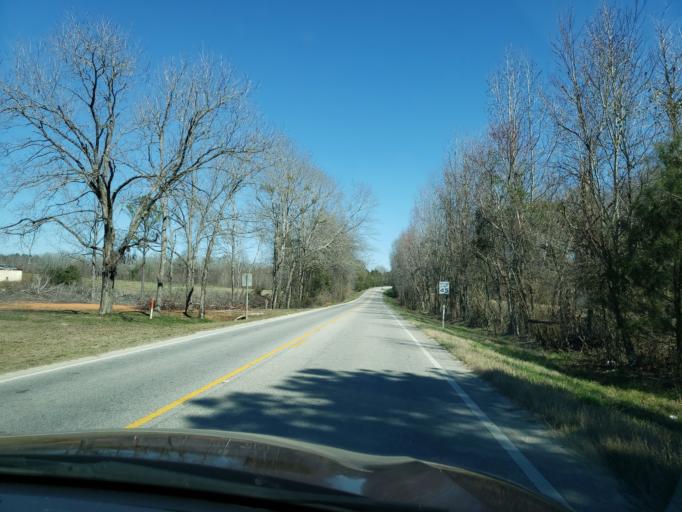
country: US
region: Alabama
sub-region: Lee County
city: Auburn
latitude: 32.6013
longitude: -85.6083
